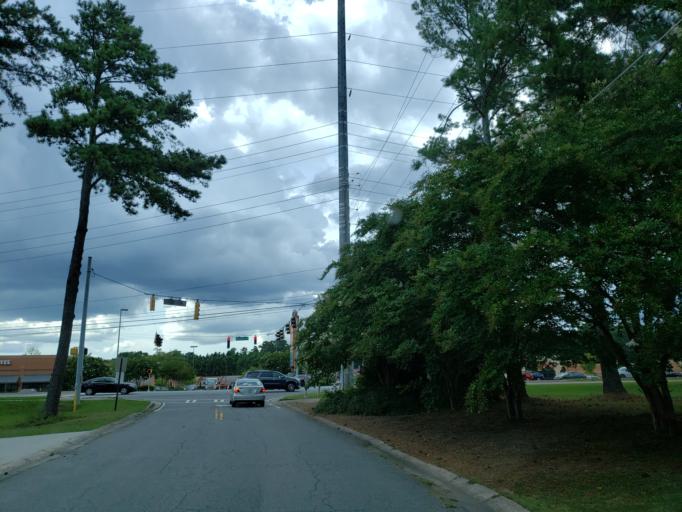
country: US
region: Georgia
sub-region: Fulton County
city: Sandy Springs
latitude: 33.9797
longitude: -84.4325
